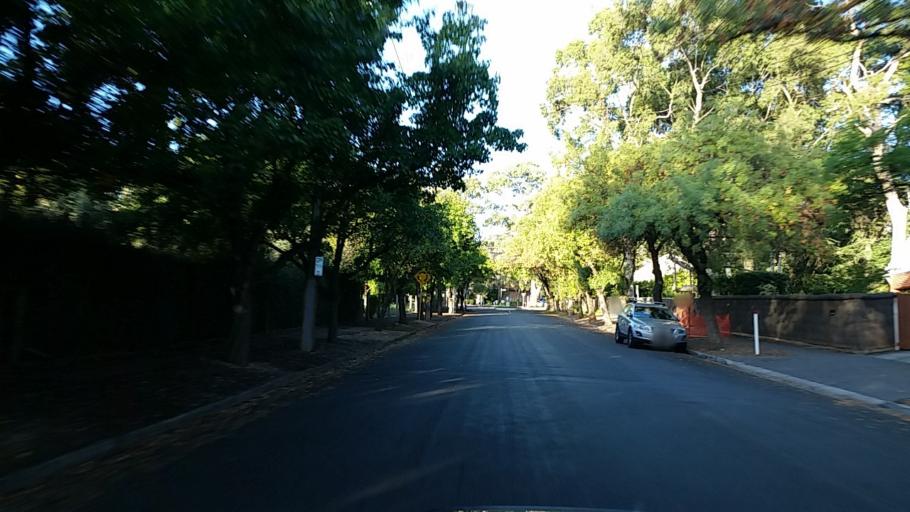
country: AU
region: South Australia
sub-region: Mitcham
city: Mitcham
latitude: -34.9704
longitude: 138.6346
